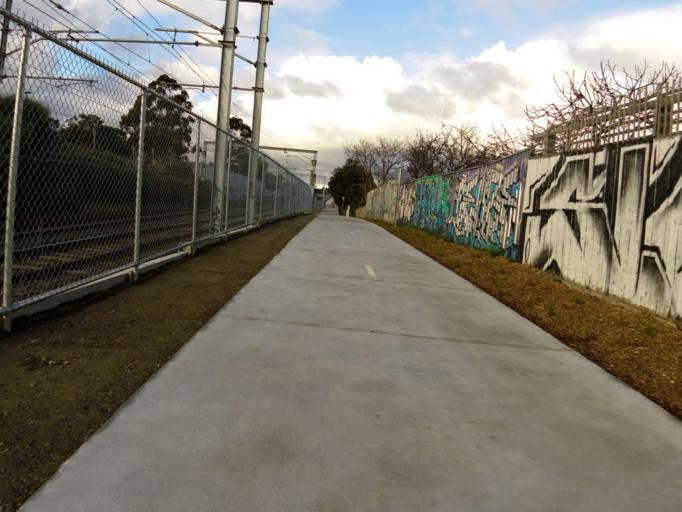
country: AU
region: Victoria
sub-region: Whitehorse
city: Nunawading
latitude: -37.8213
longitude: 145.1709
